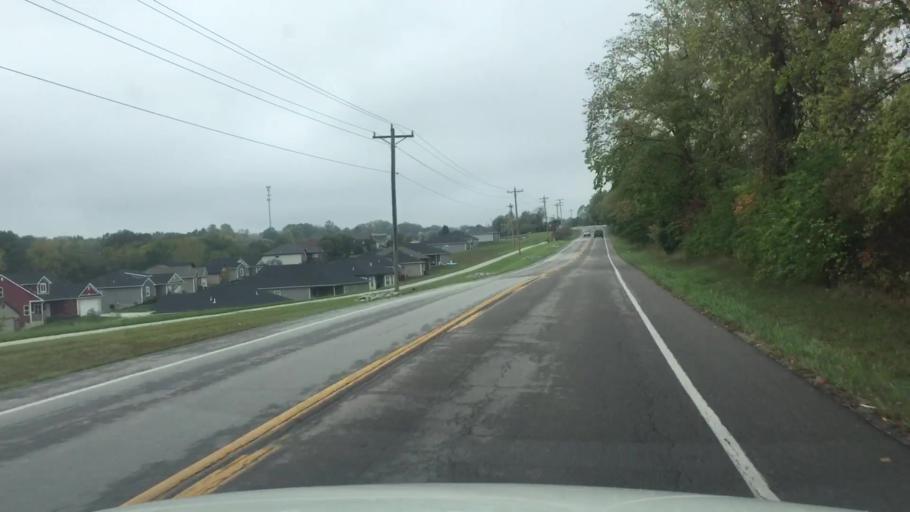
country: US
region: Missouri
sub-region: Boone County
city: Columbia
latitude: 38.8705
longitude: -92.3894
